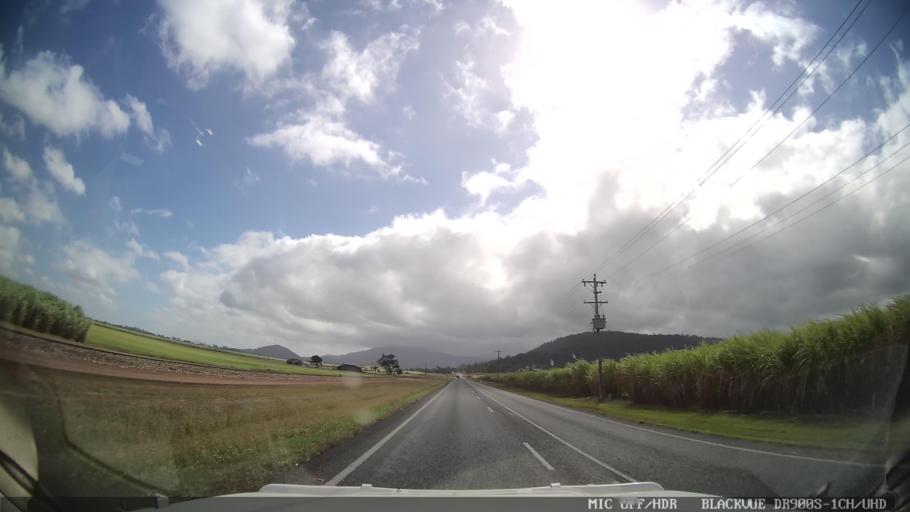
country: AU
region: Queensland
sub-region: Whitsunday
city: Red Hill
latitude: -20.3424
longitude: 148.5529
